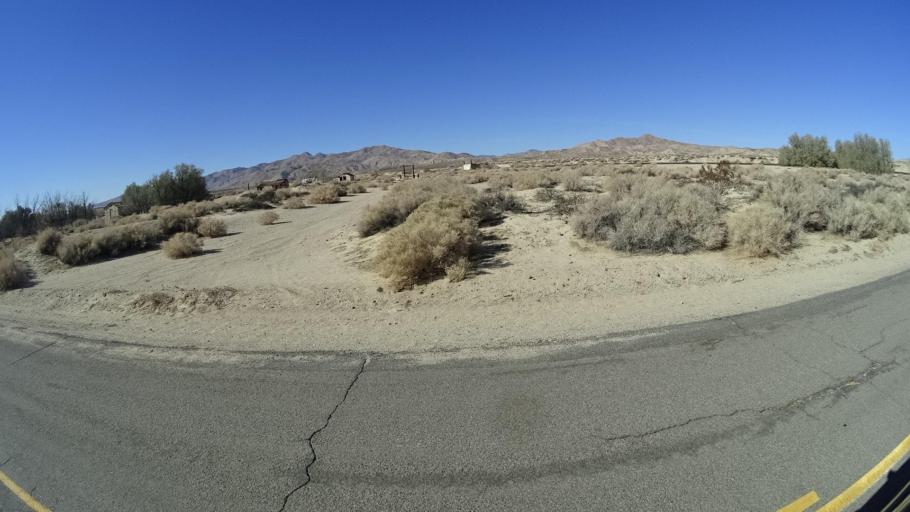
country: US
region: California
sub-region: Kern County
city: California City
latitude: 35.3081
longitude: -117.9679
